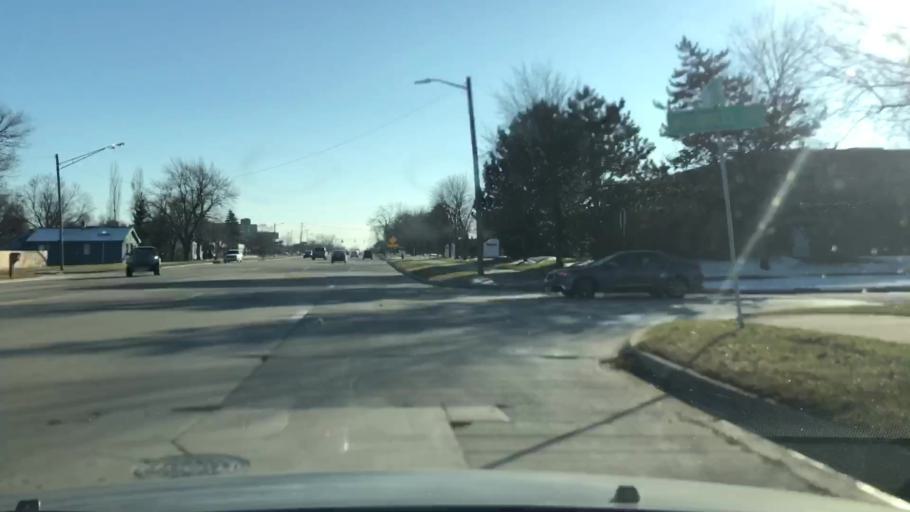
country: US
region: Michigan
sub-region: Oakland County
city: Clawson
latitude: 42.5526
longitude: -83.1079
